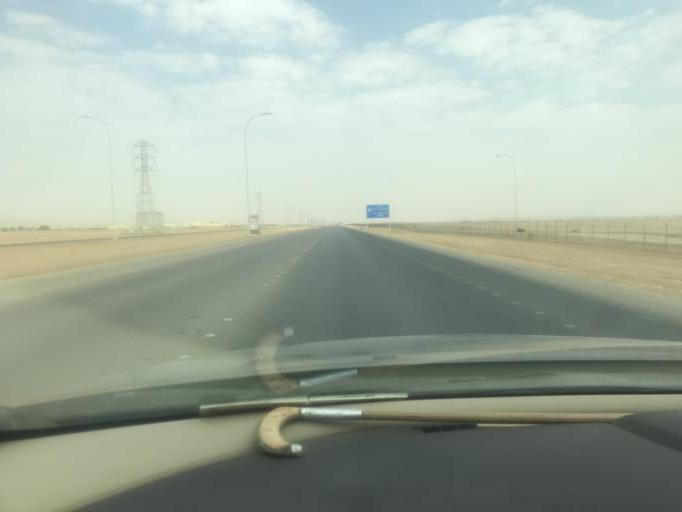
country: SA
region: Ar Riyad
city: Riyadh
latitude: 24.9212
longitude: 46.6946
